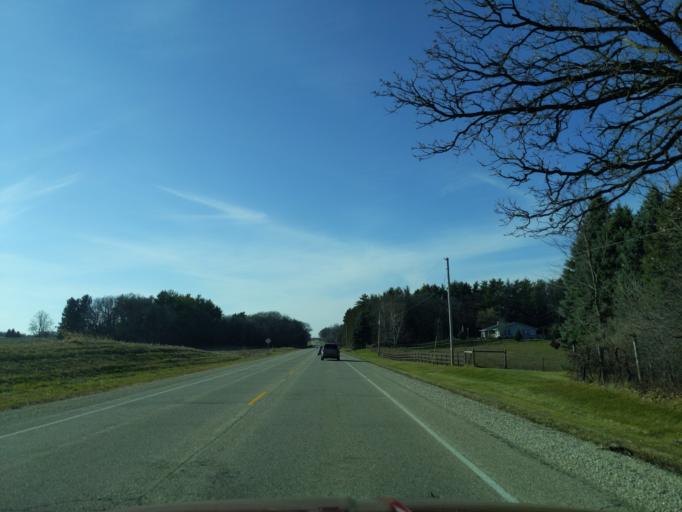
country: US
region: Wisconsin
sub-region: Rock County
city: Milton
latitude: 42.8262
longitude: -88.8875
